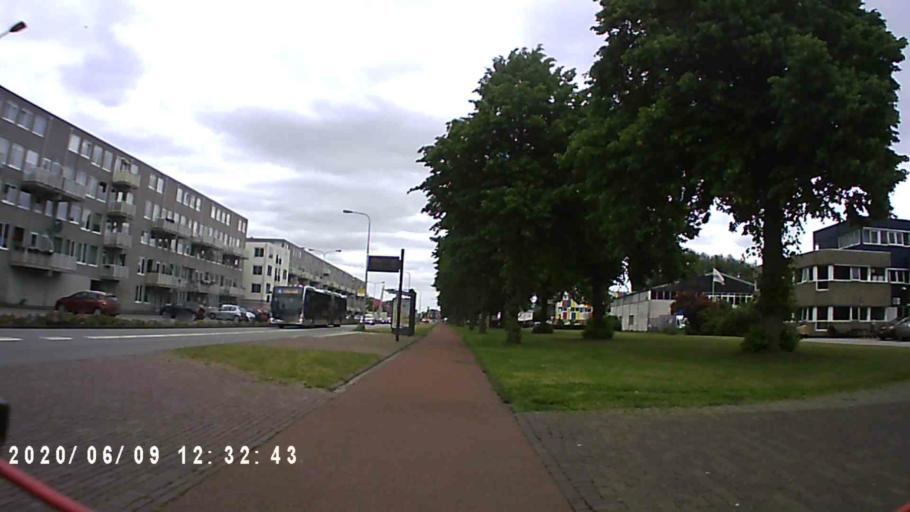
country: NL
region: Groningen
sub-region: Gemeente Groningen
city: Oosterpark
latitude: 53.2209
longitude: 6.5850
